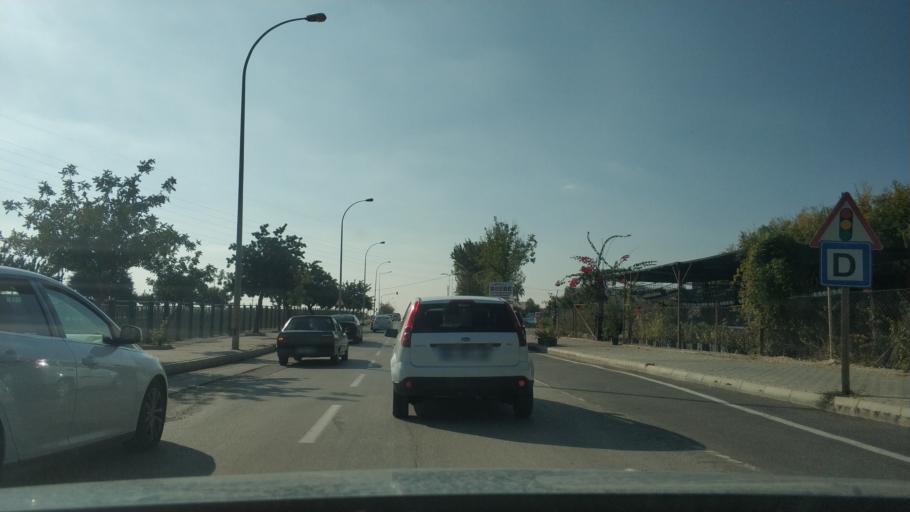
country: TR
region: Adana
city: Seyhan
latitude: 37.0063
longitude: 35.2541
